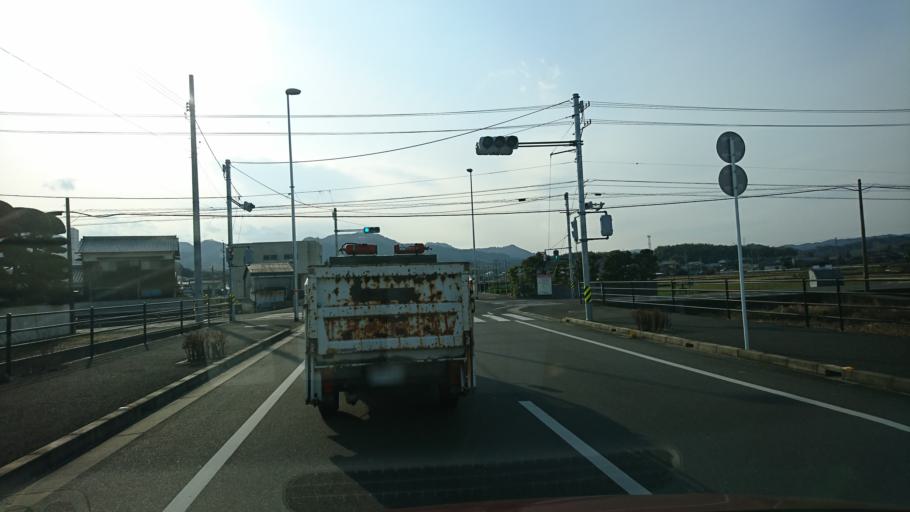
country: JP
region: Ehime
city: Saijo
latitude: 34.0255
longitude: 133.0021
